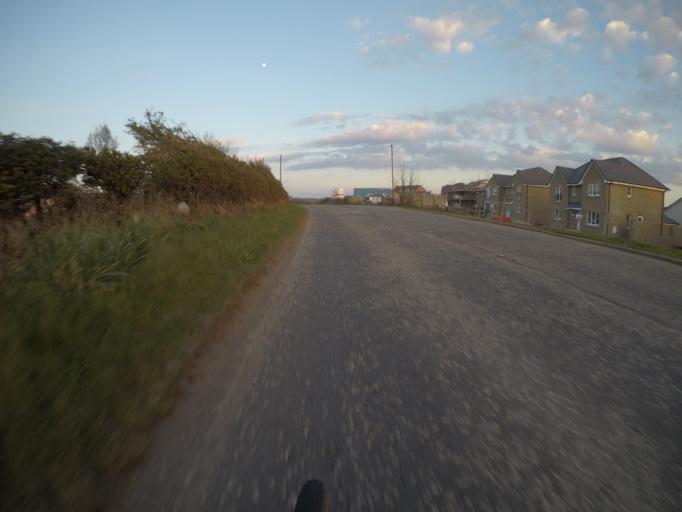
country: GB
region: Scotland
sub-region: South Ayrshire
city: Troon
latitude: 55.5634
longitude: -4.6356
